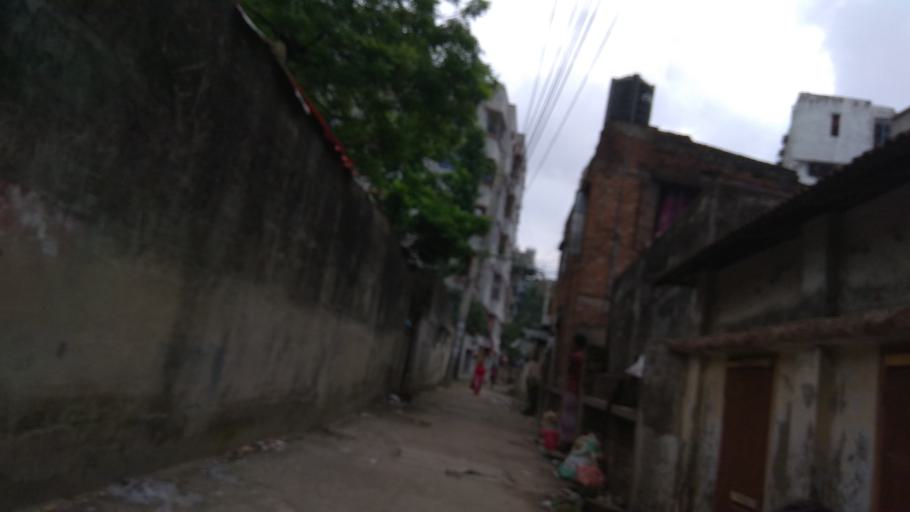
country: BD
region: Dhaka
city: Azimpur
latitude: 23.7972
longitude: 90.3611
